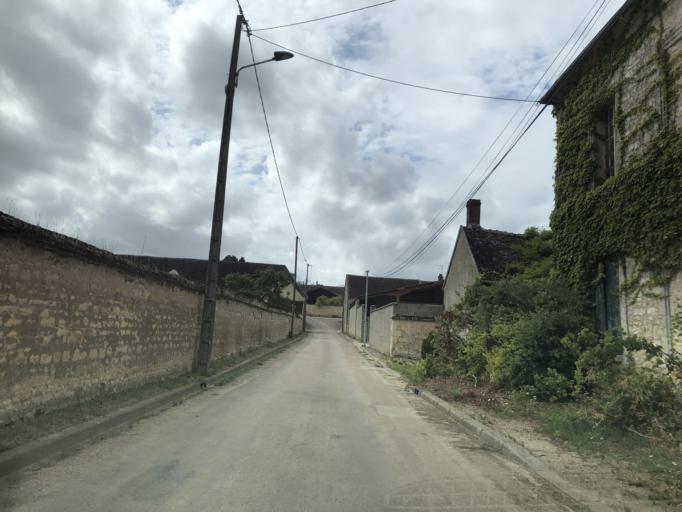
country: FR
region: Bourgogne
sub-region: Departement de l'Yonne
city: Laroche-Saint-Cydroine
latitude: 47.9478
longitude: 3.4468
